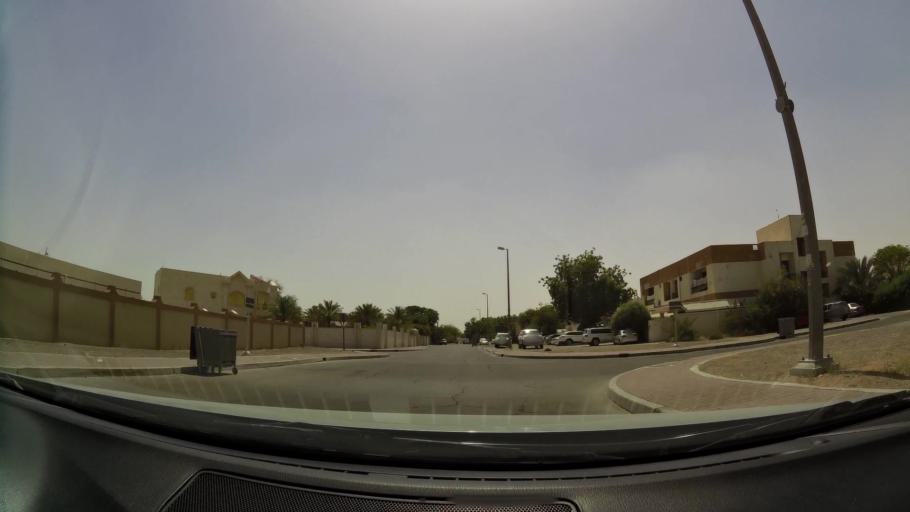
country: AE
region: Abu Dhabi
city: Al Ain
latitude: 24.2361
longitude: 55.7177
